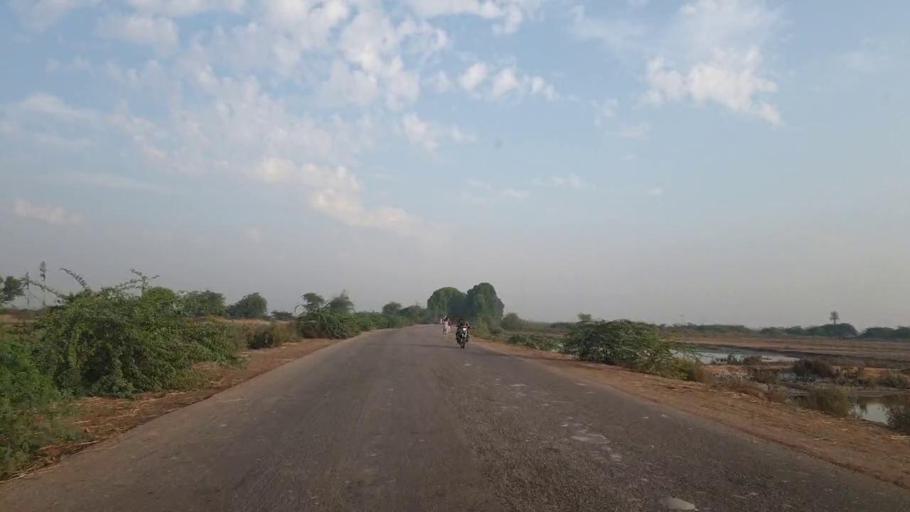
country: PK
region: Sindh
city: Tando Bago
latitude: 24.7251
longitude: 68.9425
